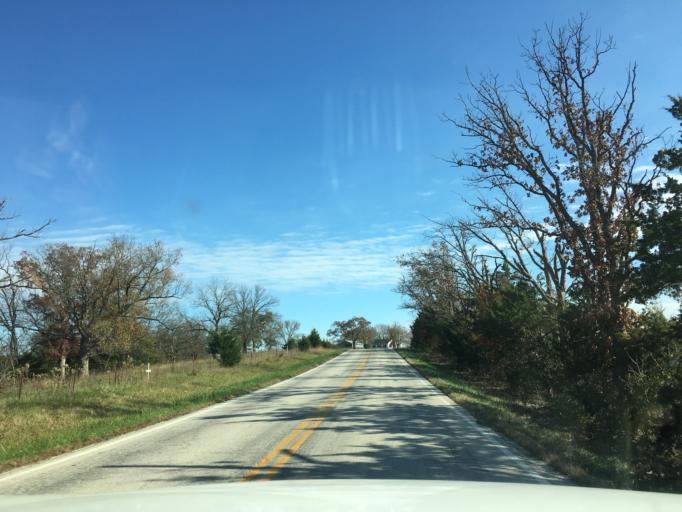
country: US
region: Missouri
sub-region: Osage County
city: Linn
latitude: 38.4382
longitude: -91.8328
